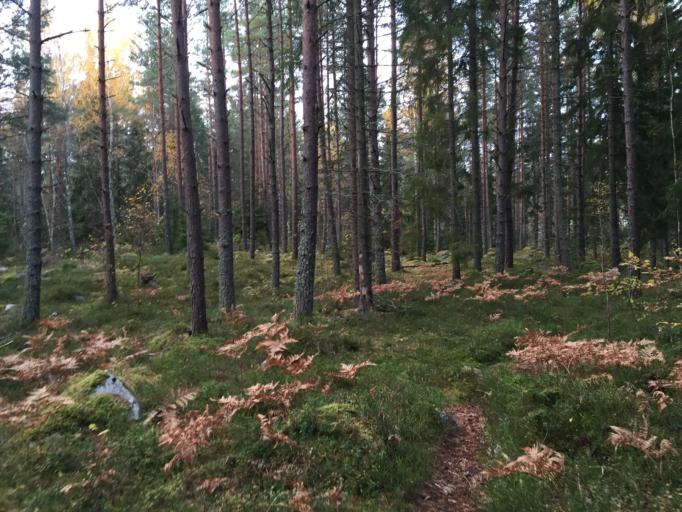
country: SE
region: Vaestmanland
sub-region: Hallstahammars Kommun
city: Hallstahammar
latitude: 59.6321
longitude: 16.2480
